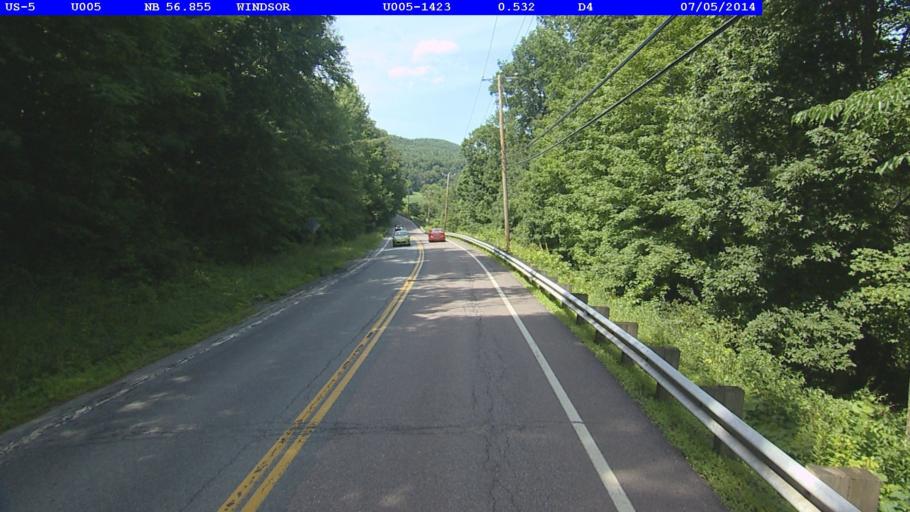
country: US
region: Vermont
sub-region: Windsor County
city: Windsor
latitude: 43.4364
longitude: -72.3966
